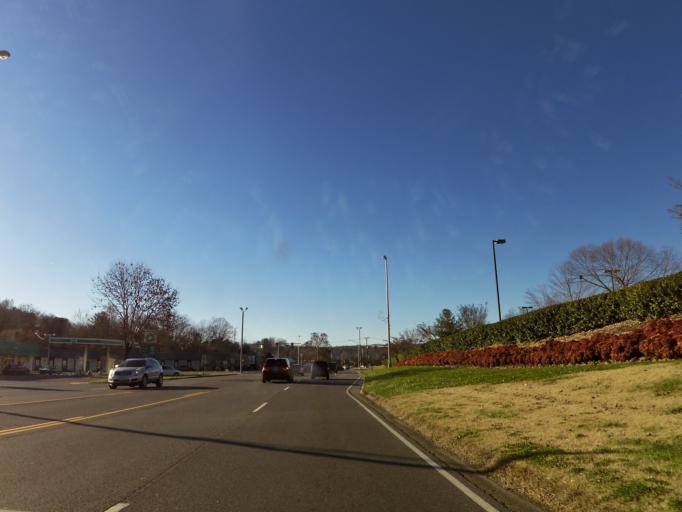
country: US
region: Tennessee
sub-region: Anderson County
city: Oak Ridge
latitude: 36.0077
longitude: -84.2622
